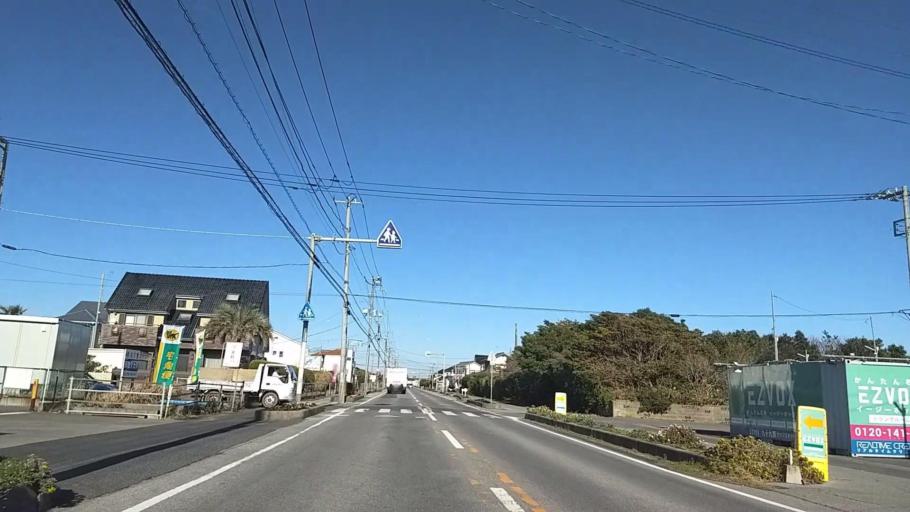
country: JP
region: Chiba
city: Togane
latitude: 35.5103
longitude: 140.4353
